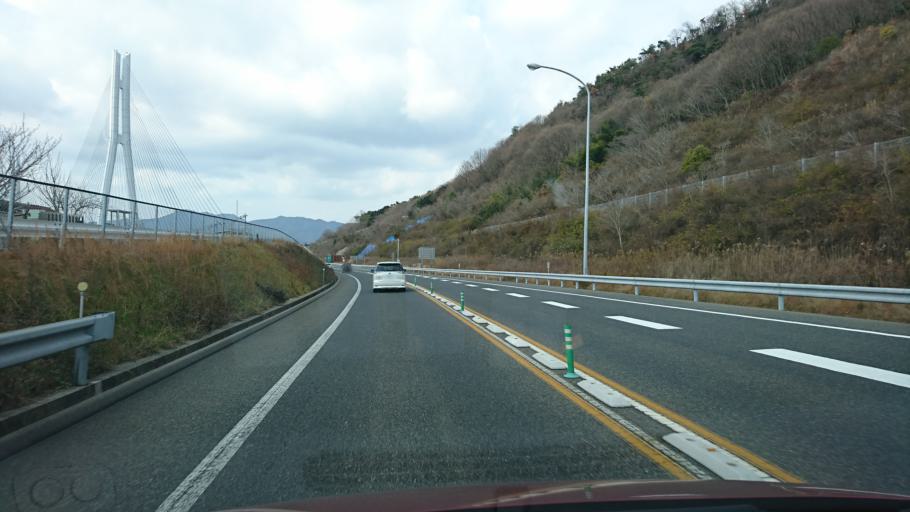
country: JP
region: Hiroshima
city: Innoshima
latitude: 34.2608
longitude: 133.0763
